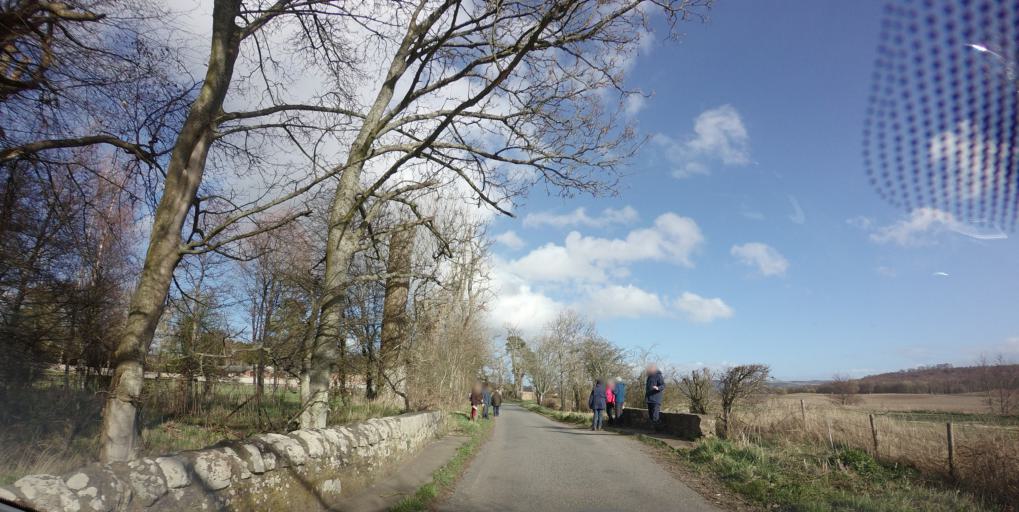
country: GB
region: Scotland
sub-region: Perth and Kinross
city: Bridge of Earn
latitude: 56.3379
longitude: -3.4249
